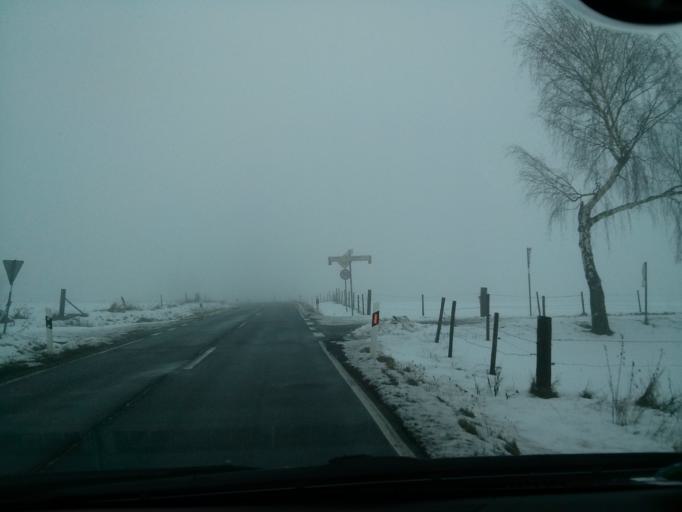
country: DE
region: Rheinland-Pfalz
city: Berg
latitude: 50.5737
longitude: 6.9460
